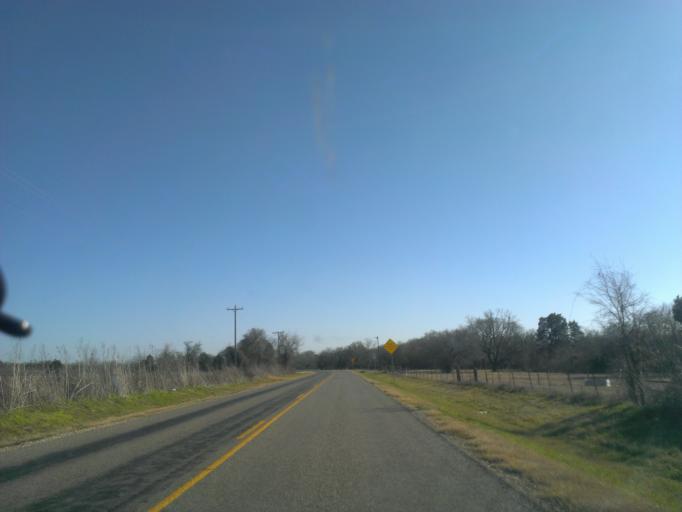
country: US
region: Texas
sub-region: Bastrop County
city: Elgin
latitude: 30.4459
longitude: -97.2639
